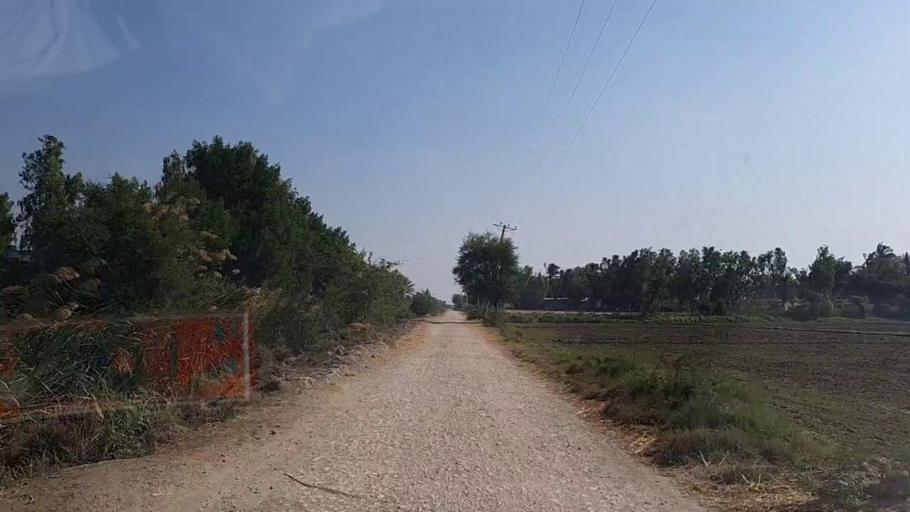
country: PK
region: Sindh
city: Thatta
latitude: 24.7988
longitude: 67.9696
